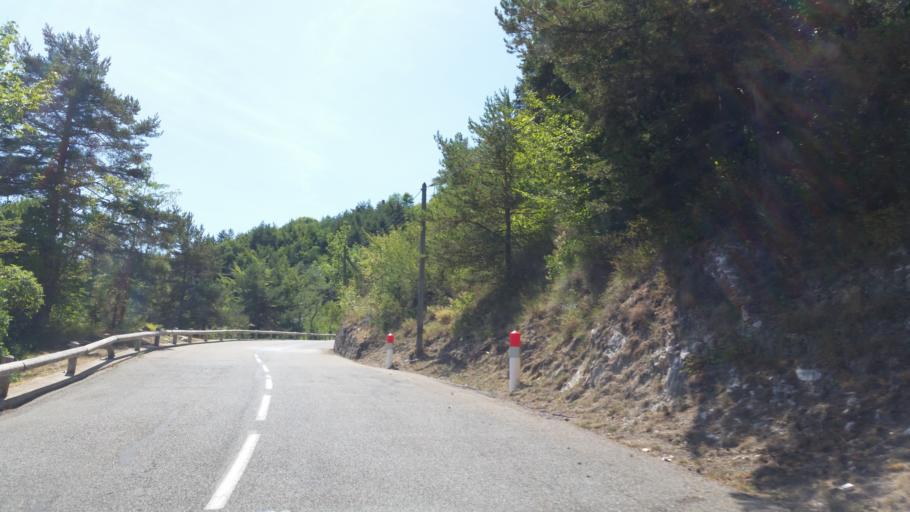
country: FR
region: Provence-Alpes-Cote d'Azur
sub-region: Departement des Alpes-Maritimes
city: Breil-sur-Roya
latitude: 43.9270
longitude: 7.4736
